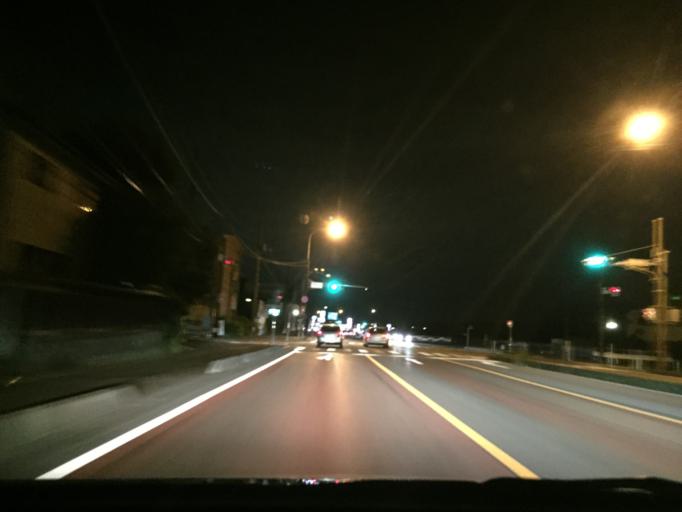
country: JP
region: Shizuoka
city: Mishima
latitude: 35.2076
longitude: 138.9171
